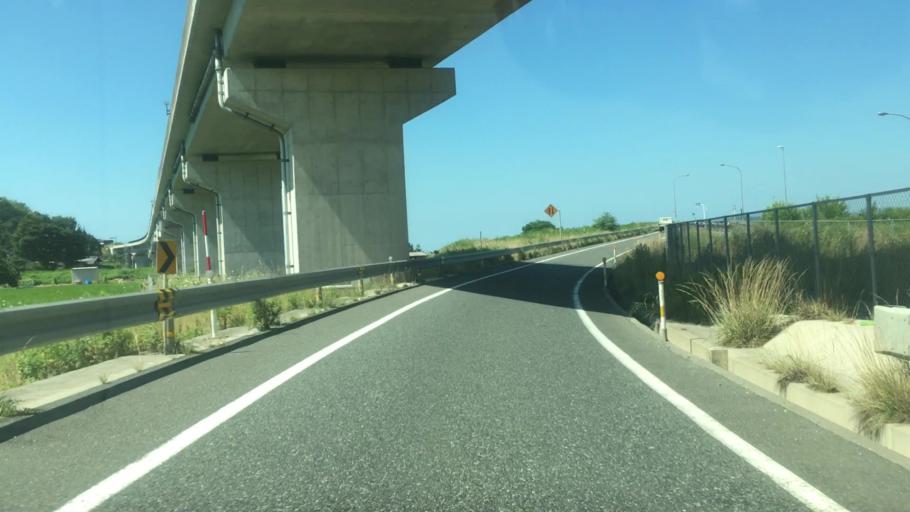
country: JP
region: Tottori
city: Tottori
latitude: 35.4348
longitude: 134.2045
